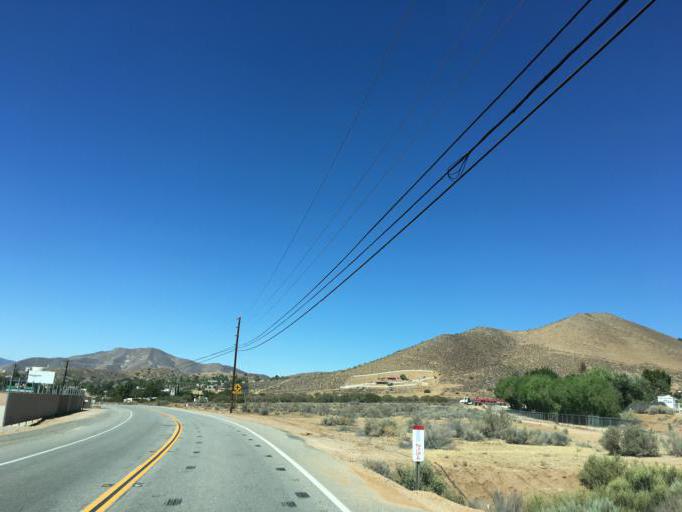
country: US
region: California
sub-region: Los Angeles County
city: Acton
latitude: 34.4808
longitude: -118.1648
